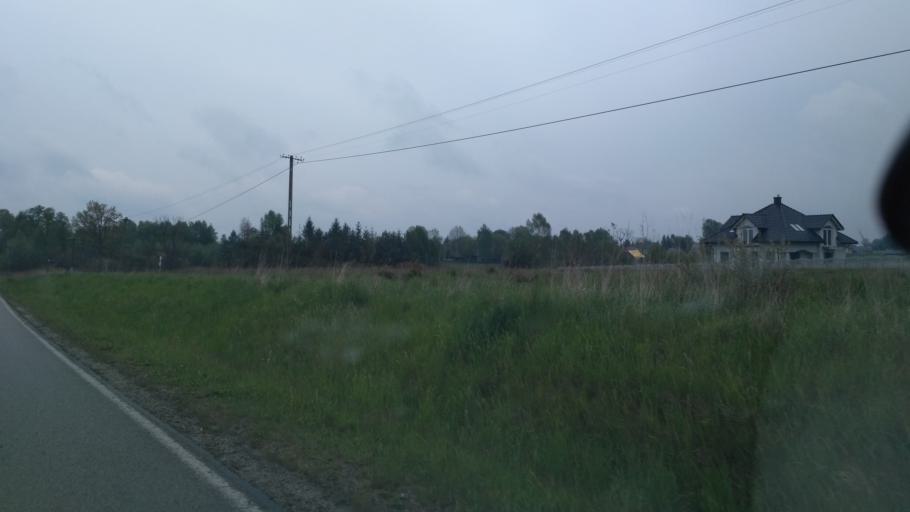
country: PL
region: Subcarpathian Voivodeship
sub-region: Powiat ropczycko-sedziszowski
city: Sedziszow Malopolski
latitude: 50.0920
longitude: 21.7293
